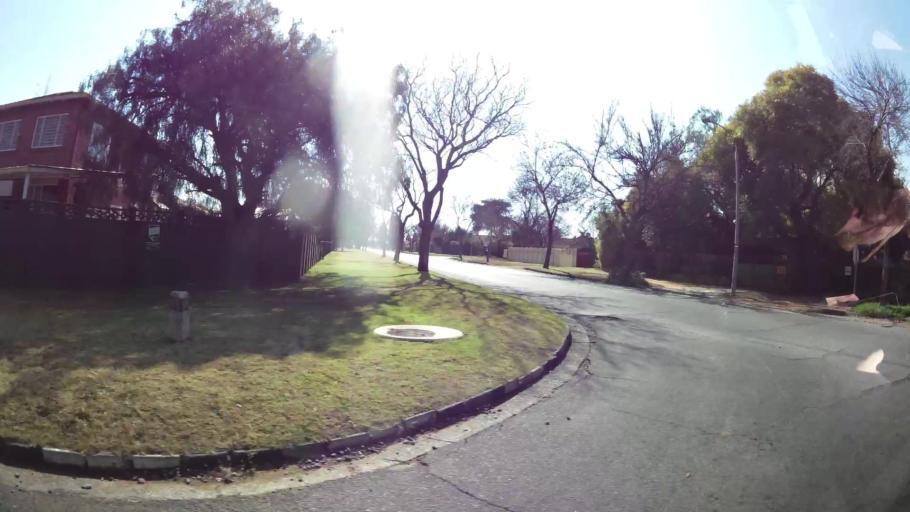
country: ZA
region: Gauteng
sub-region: Ekurhuleni Metropolitan Municipality
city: Boksburg
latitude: -26.1657
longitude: 28.2657
